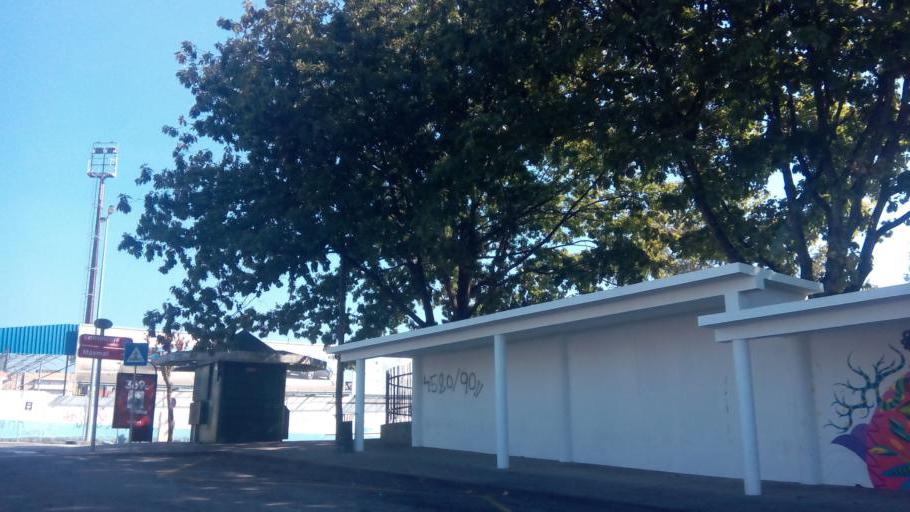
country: PT
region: Porto
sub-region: Paredes
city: Casteloes de Cepeda
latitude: 41.2030
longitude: -8.3342
